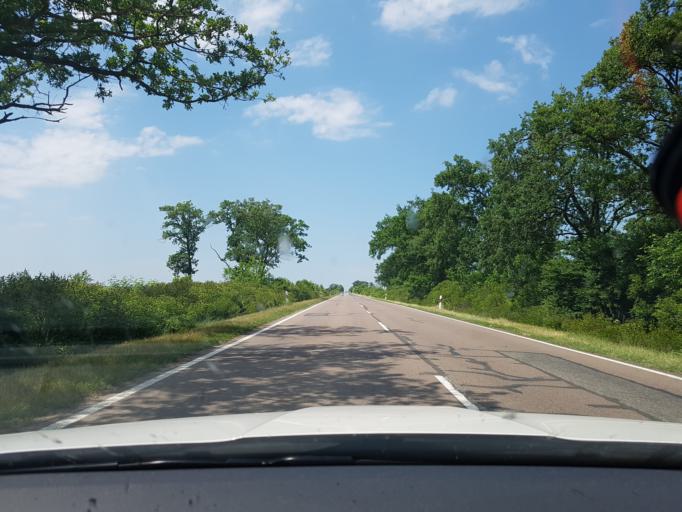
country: HU
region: Hajdu-Bihar
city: Hortobagy
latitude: 47.5860
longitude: 21.1123
